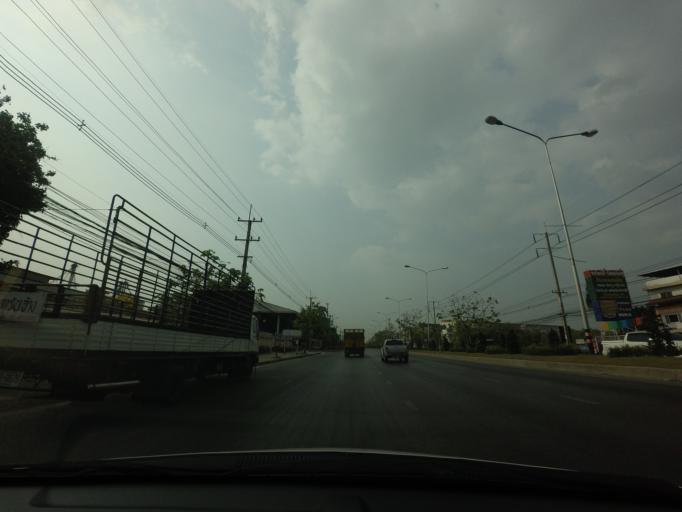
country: TH
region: Bangkok
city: Thawi Watthana
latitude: 13.7451
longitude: 100.3294
